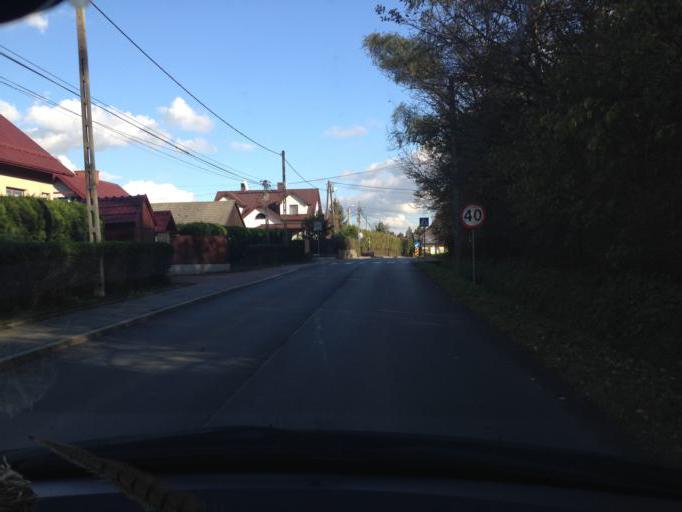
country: PL
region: Lesser Poland Voivodeship
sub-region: Powiat krakowski
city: Rzaska
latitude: 50.0680
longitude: 19.8268
